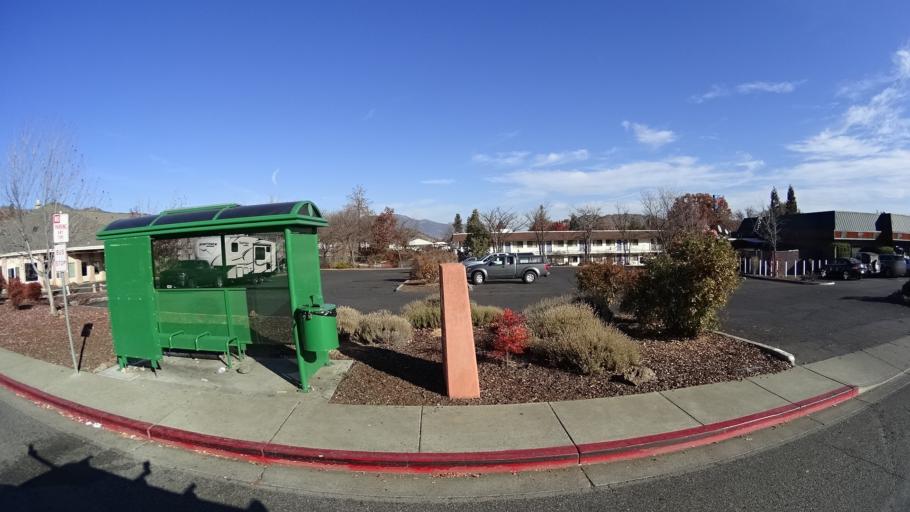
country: US
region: California
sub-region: Siskiyou County
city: Yreka
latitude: 41.7040
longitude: -122.6459
